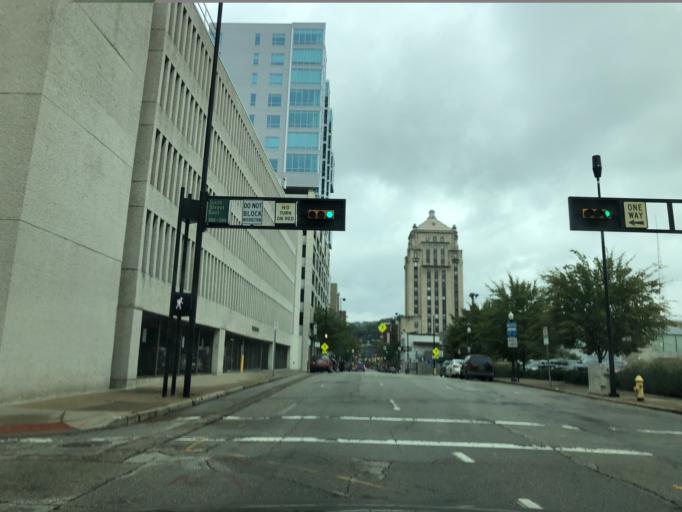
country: US
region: Kentucky
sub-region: Campbell County
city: Newport
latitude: 39.1033
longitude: -84.5069
